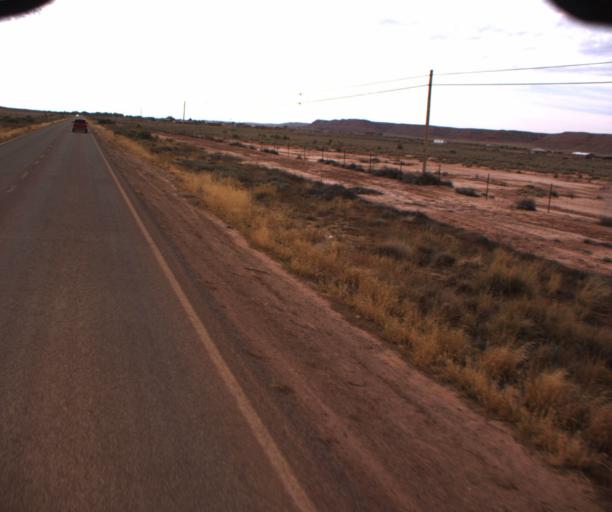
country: US
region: Arizona
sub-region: Apache County
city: Many Farms
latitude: 36.2886
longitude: -109.6043
